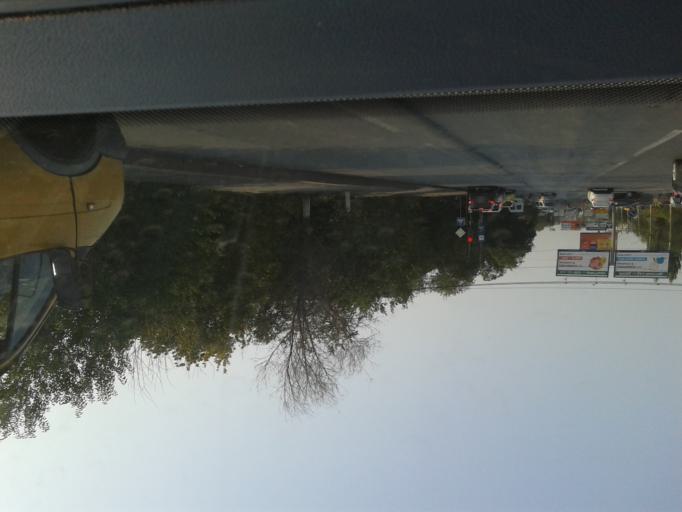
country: RU
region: Volgograd
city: Volgograd
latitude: 48.6558
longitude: 44.4371
